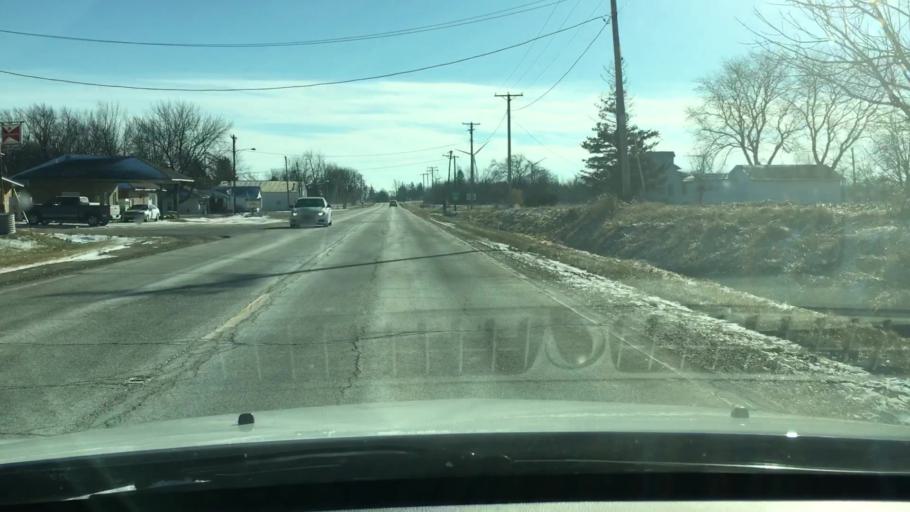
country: US
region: Illinois
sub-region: LaSalle County
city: Mendota
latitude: 41.6957
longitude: -89.0914
